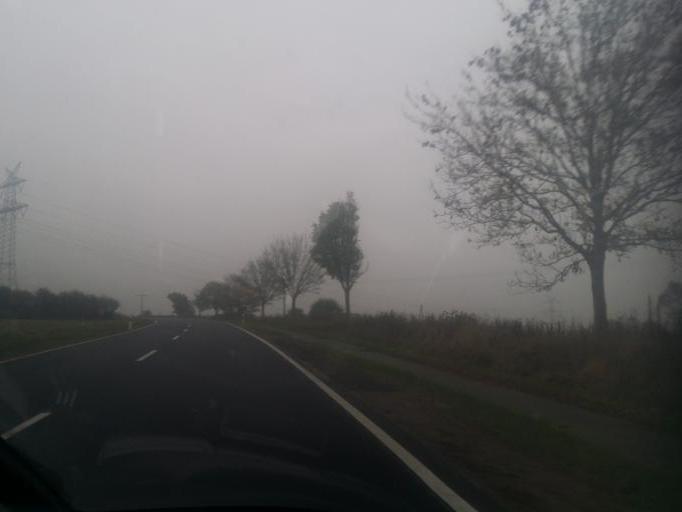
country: DE
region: Schleswig-Holstein
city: Tarp
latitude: 54.6652
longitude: 9.4166
